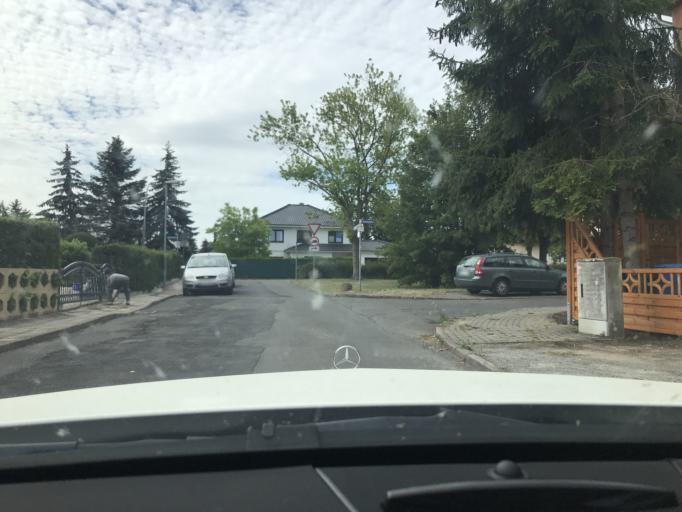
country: DE
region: Thuringia
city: Muehlhausen
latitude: 51.2020
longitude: 10.4745
